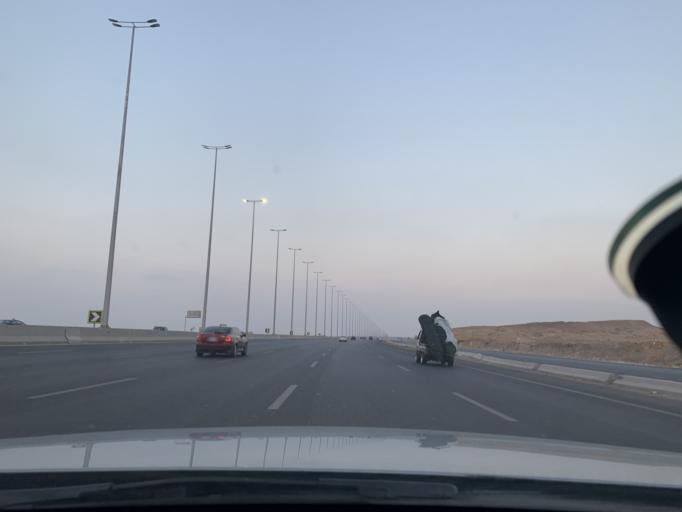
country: EG
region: Muhafazat al Qalyubiyah
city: Al Khankah
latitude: 30.0943
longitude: 31.4889
